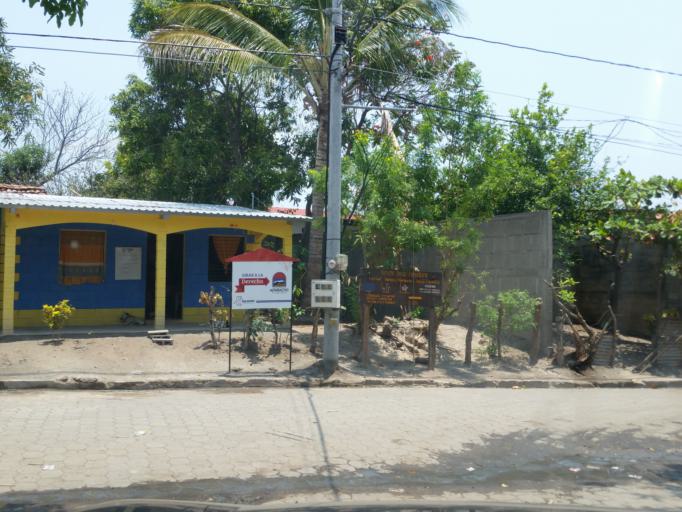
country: NI
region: Granada
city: Granada
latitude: 11.9127
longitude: -85.9540
